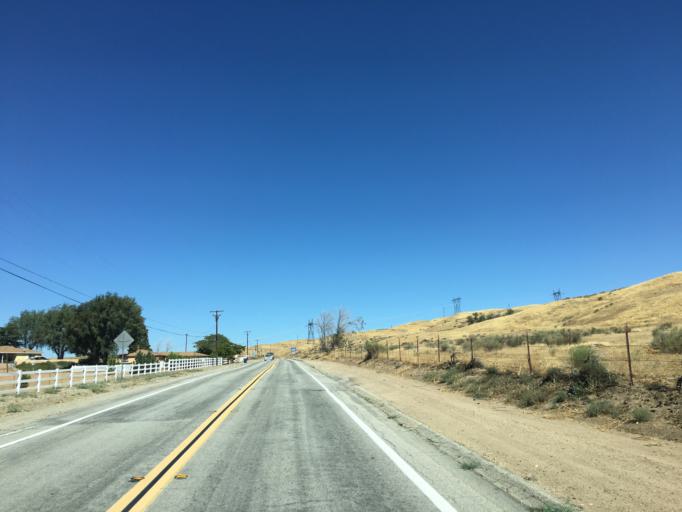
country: US
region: California
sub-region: Los Angeles County
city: Leona Valley
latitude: 34.6326
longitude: -118.3354
